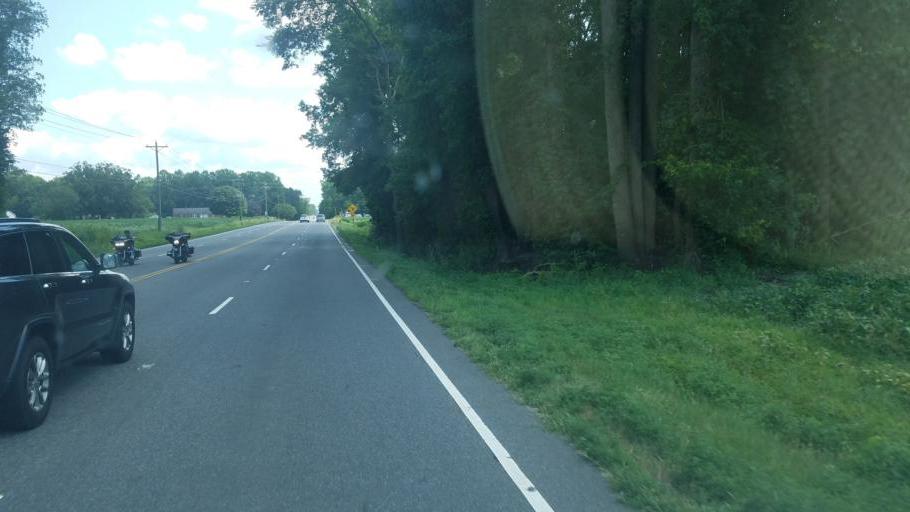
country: US
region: Virginia
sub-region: Isle of Wight County
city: Windsor
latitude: 36.8328
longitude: -76.7814
